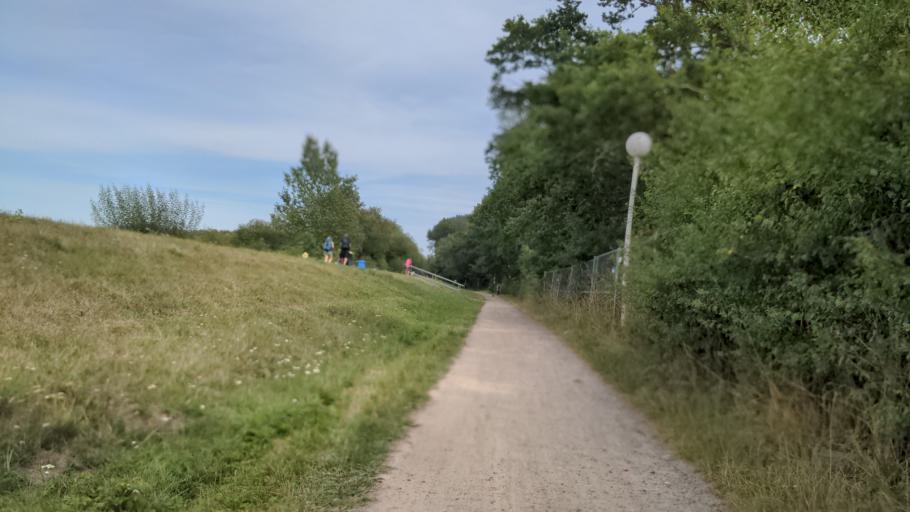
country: DE
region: Mecklenburg-Vorpommern
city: Ostseebad Boltenhagen
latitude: 53.9811
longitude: 11.2356
